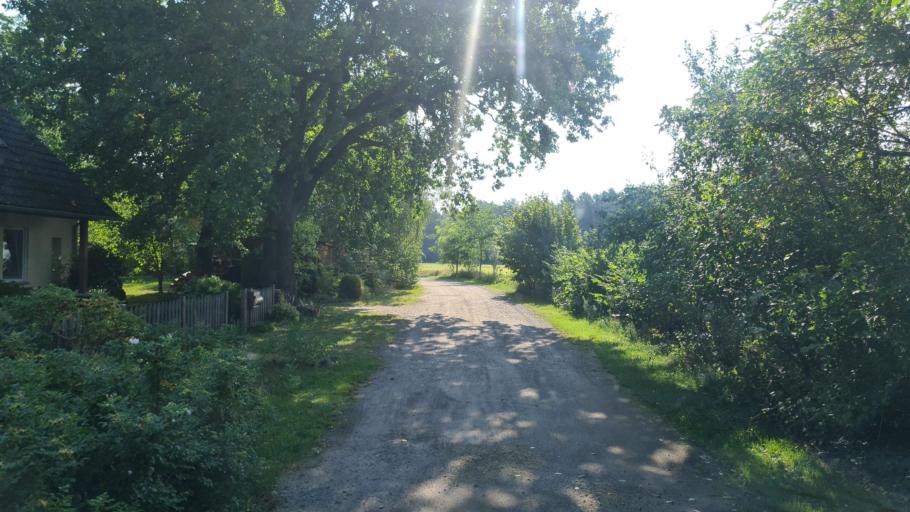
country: DE
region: Brandenburg
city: Drebkau
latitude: 51.6927
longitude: 14.1733
